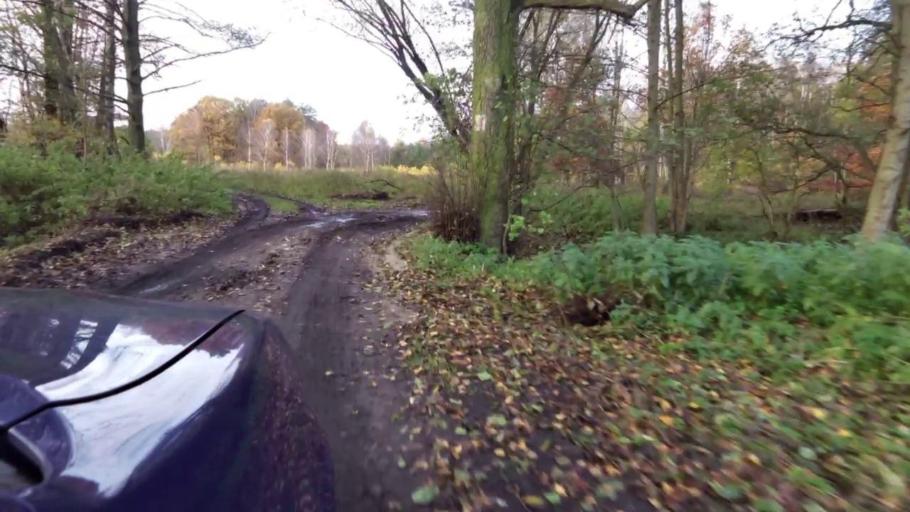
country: PL
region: West Pomeranian Voivodeship
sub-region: Powiat goleniowski
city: Goleniow
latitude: 53.6091
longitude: 14.7530
